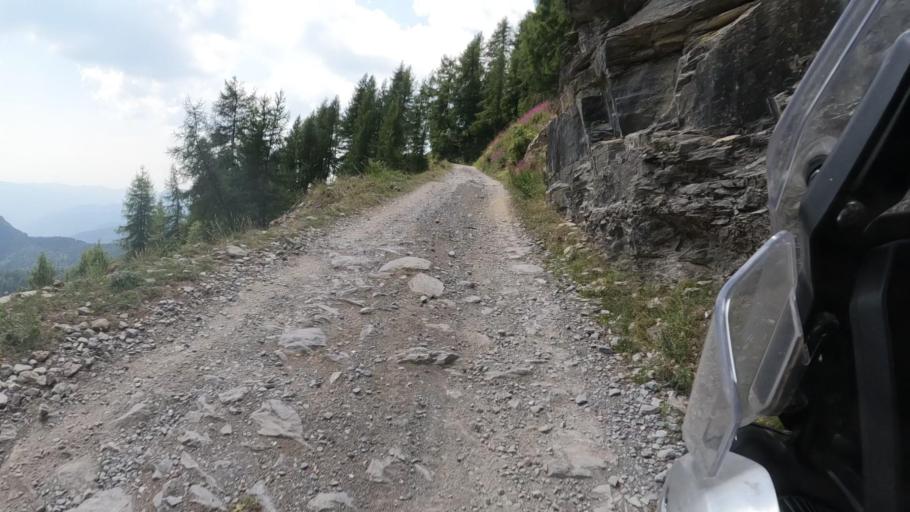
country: IT
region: Liguria
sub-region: Provincia di Imperia
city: Pigna
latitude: 44.0178
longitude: 7.6625
